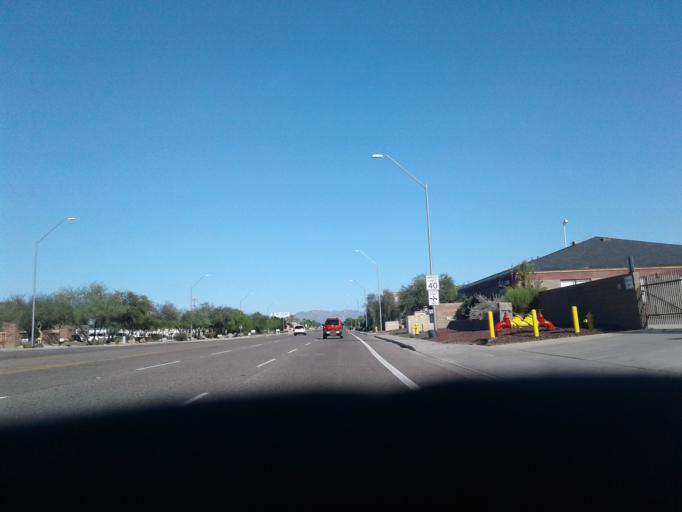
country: US
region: Arizona
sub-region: Maricopa County
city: Cave Creek
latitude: 33.6878
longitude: -112.0475
